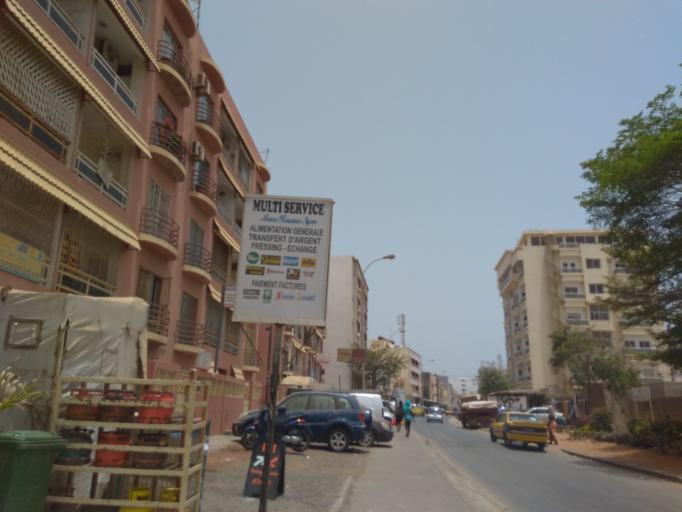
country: SN
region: Dakar
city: Grand Dakar
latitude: 14.7294
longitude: -17.4631
